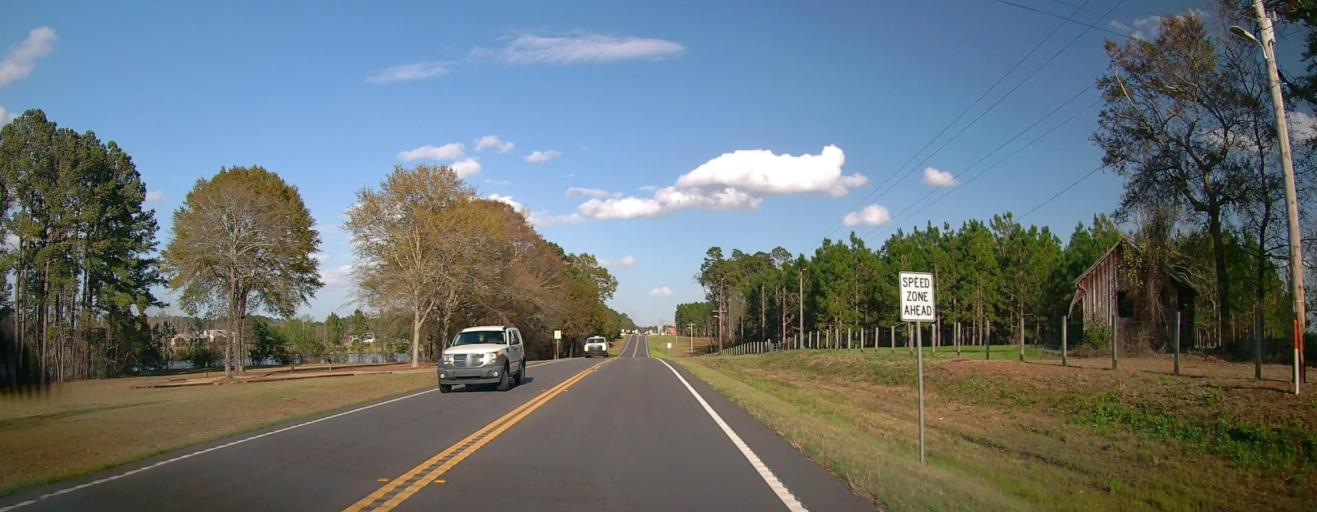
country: US
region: Georgia
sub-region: Toombs County
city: Vidalia
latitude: 32.2093
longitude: -82.4701
